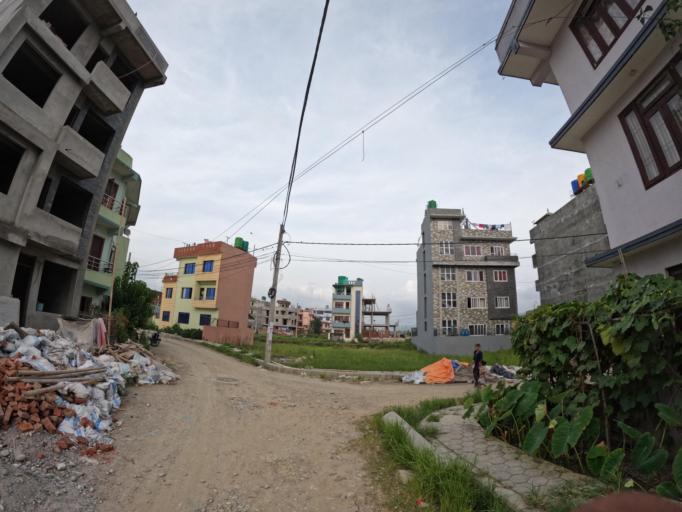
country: NP
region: Central Region
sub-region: Bagmati Zone
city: Bhaktapur
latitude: 27.6777
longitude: 85.3929
